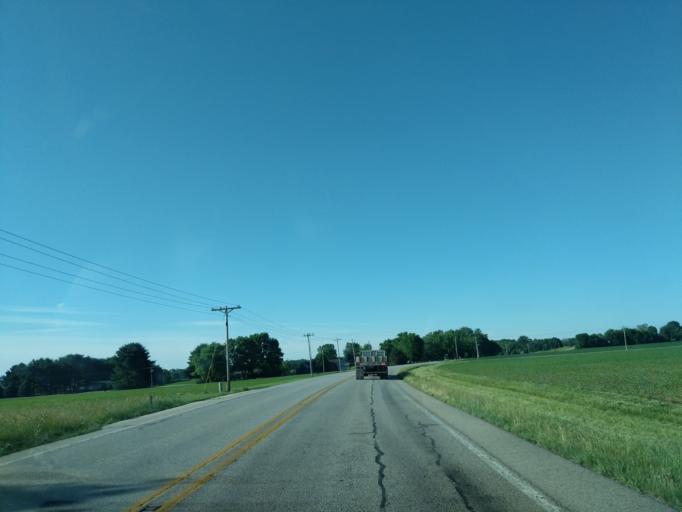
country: US
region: Indiana
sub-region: Shelby County
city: Morristown
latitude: 39.6133
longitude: -85.7669
